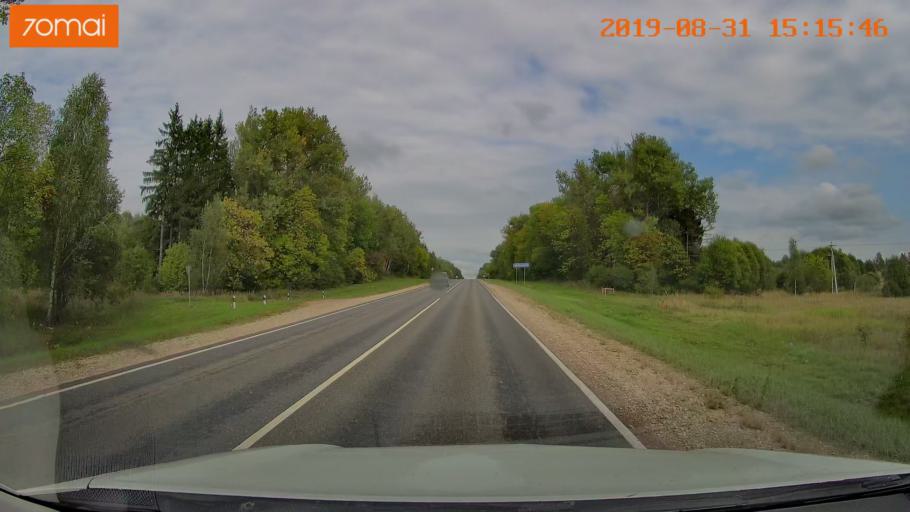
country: RU
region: Kaluga
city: Baryatino
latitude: 54.4543
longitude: 34.3343
